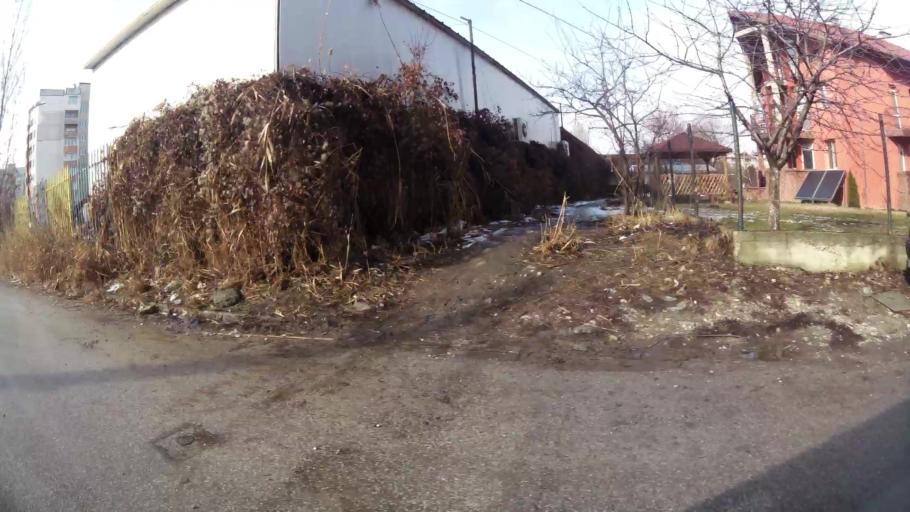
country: BG
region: Sofia-Capital
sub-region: Stolichna Obshtina
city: Sofia
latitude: 42.7238
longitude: 23.2642
